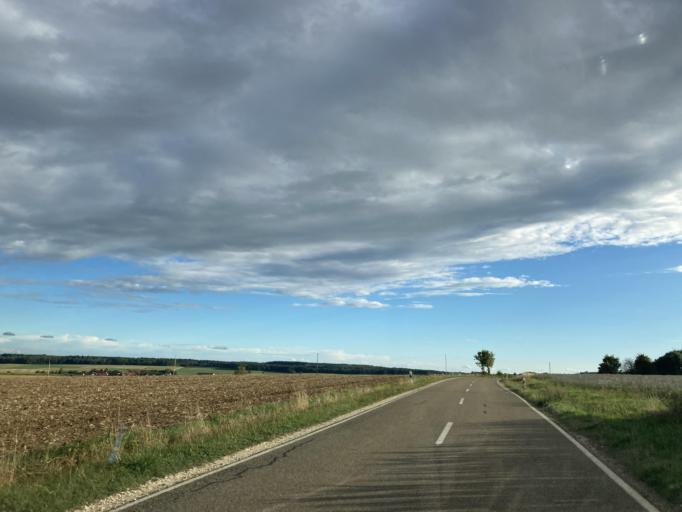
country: DE
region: Bavaria
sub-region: Swabia
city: Amerdingen
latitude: 48.7261
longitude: 10.4492
